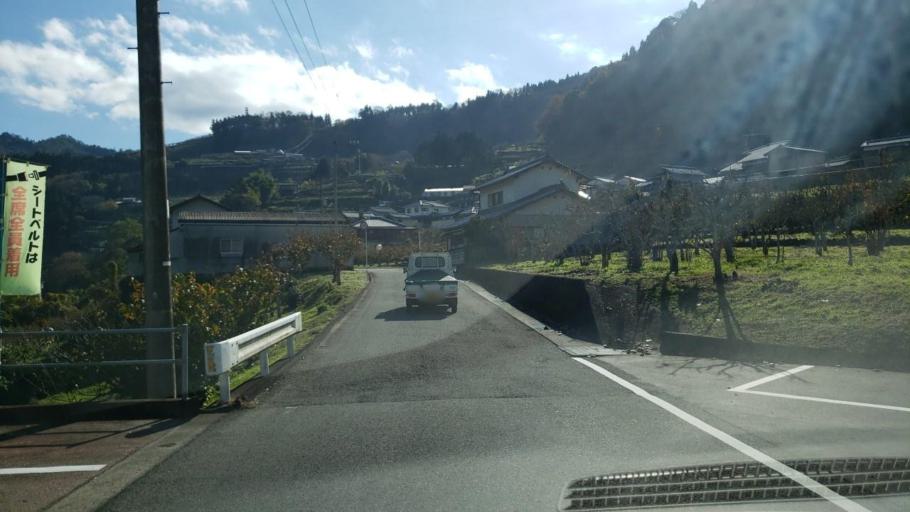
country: JP
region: Tokushima
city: Wakimachi
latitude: 34.0258
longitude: 134.0295
